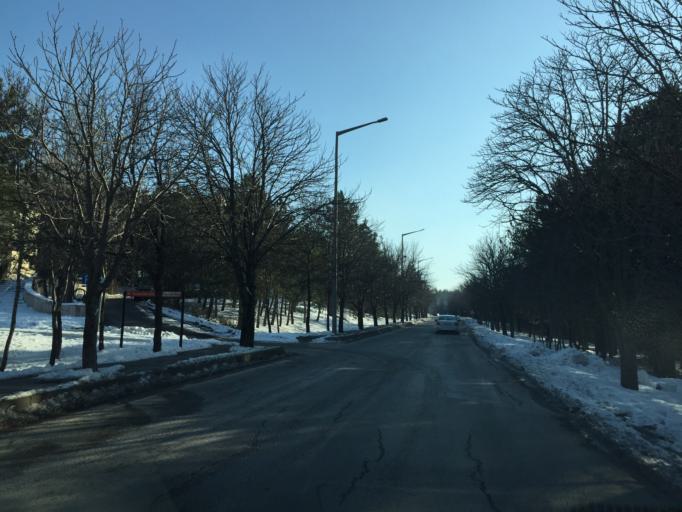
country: TR
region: Ankara
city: Ankara
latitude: 39.8889
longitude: 32.7815
